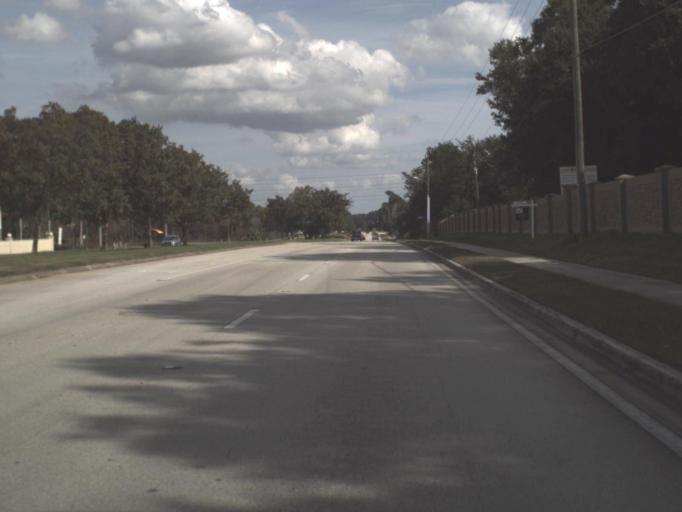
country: US
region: Florida
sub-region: Seminole County
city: Lake Mary
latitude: 28.7563
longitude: -81.3049
